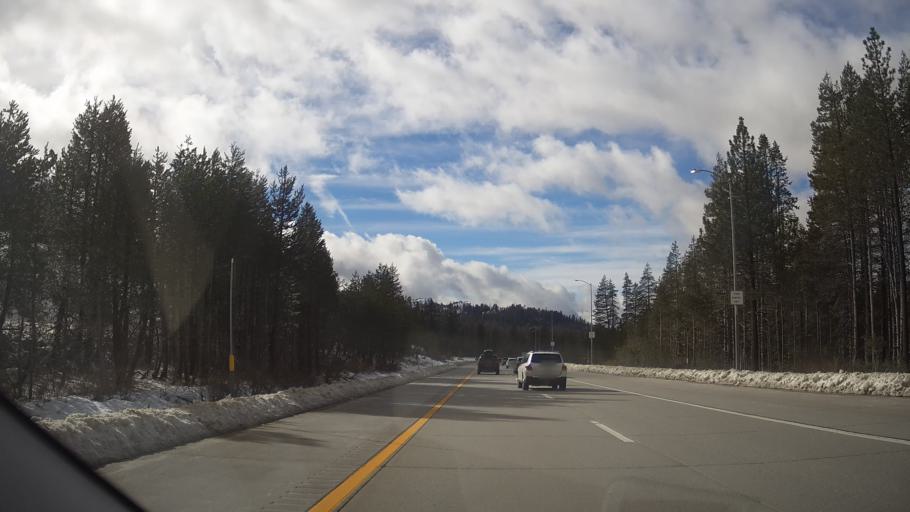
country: US
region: California
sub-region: Nevada County
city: Truckee
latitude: 39.3150
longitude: -120.4646
